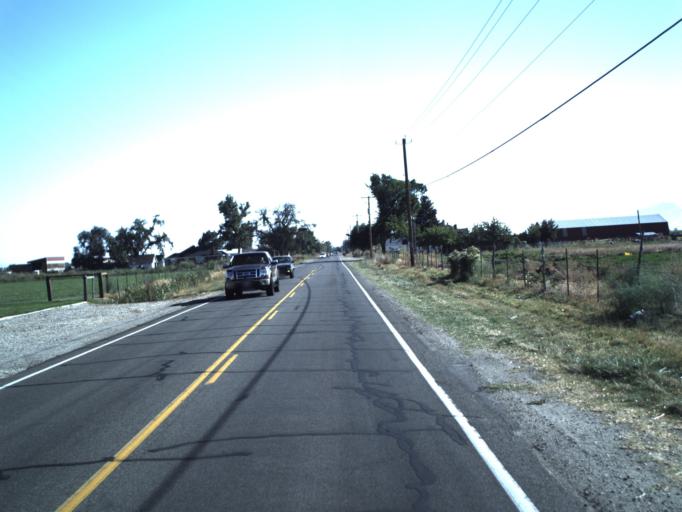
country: US
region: Utah
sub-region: Weber County
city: Hooper
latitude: 41.1559
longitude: -112.1229
